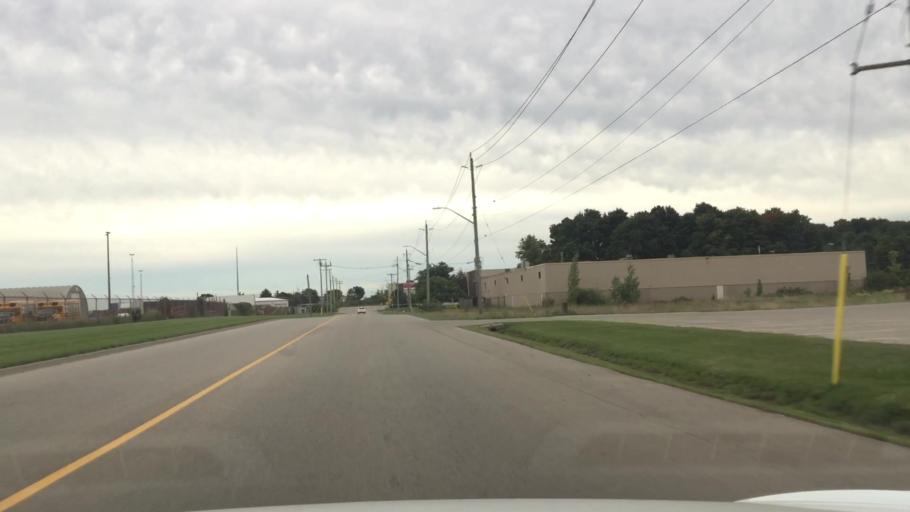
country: CA
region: Ontario
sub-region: Oxford County
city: Woodstock
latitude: 43.1199
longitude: -80.7241
